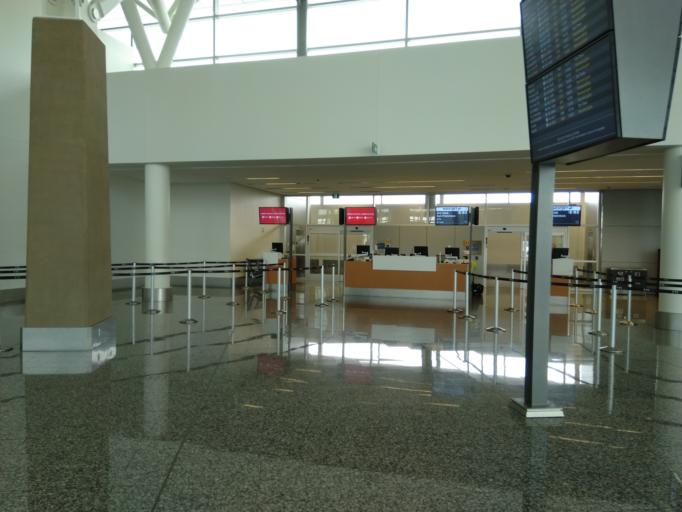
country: CA
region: Alberta
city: Calgary
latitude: 51.1300
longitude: -114.0022
